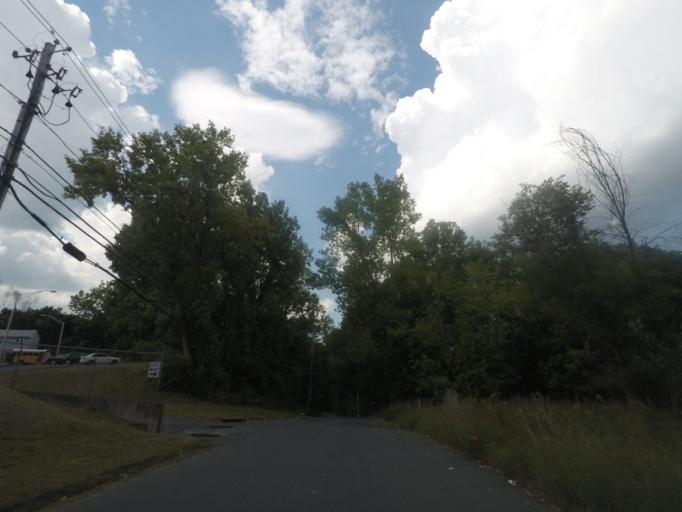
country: US
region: New York
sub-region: Rensselaer County
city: Troy
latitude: 42.7069
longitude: -73.6948
